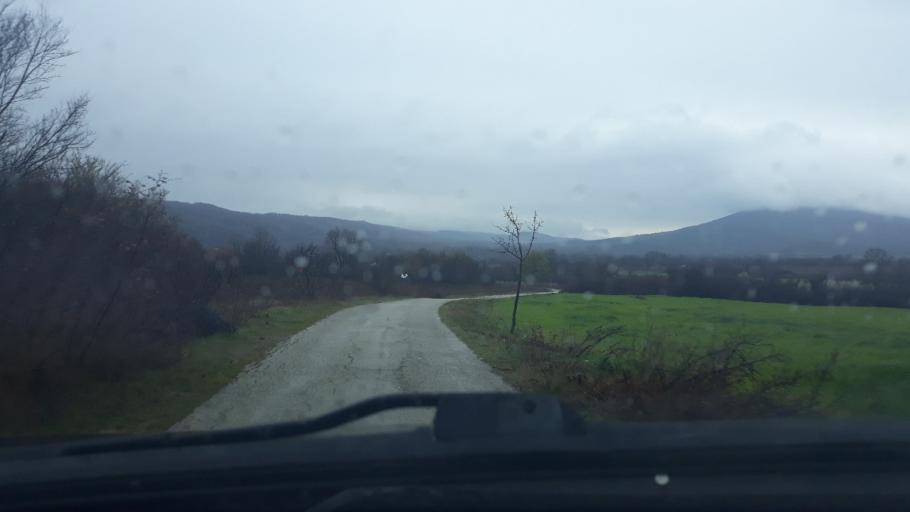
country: MK
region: Bogdanci
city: Bogdanci
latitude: 41.2377
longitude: 22.6475
